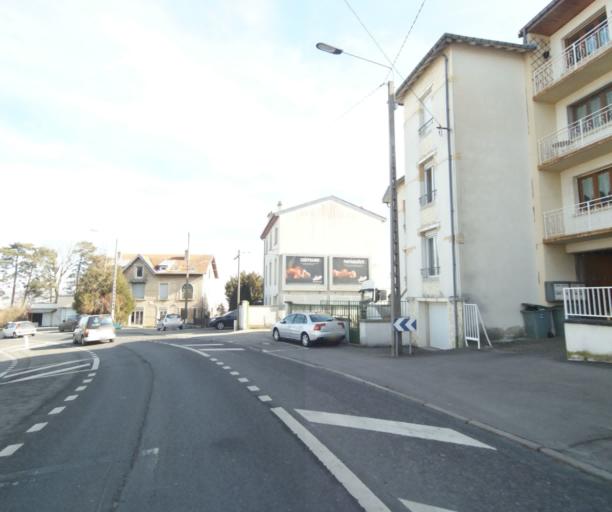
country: FR
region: Lorraine
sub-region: Departement de Meurthe-et-Moselle
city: Villers-les-Nancy
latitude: 48.6608
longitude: 6.1655
